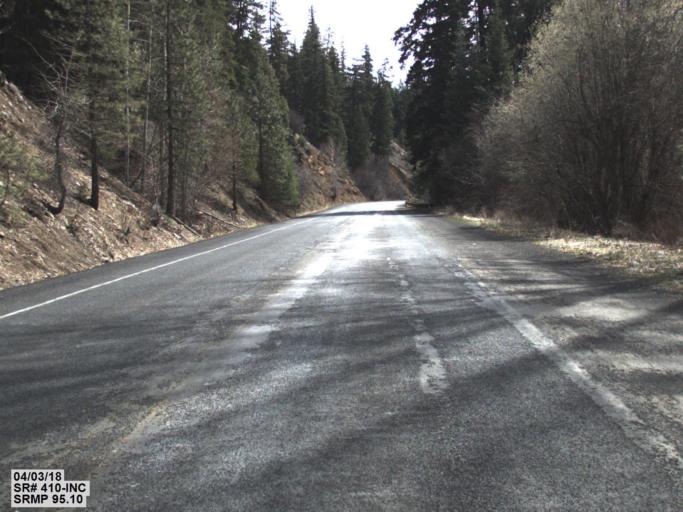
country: US
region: Washington
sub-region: Kittitas County
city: Cle Elum
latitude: 46.9547
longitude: -121.0737
